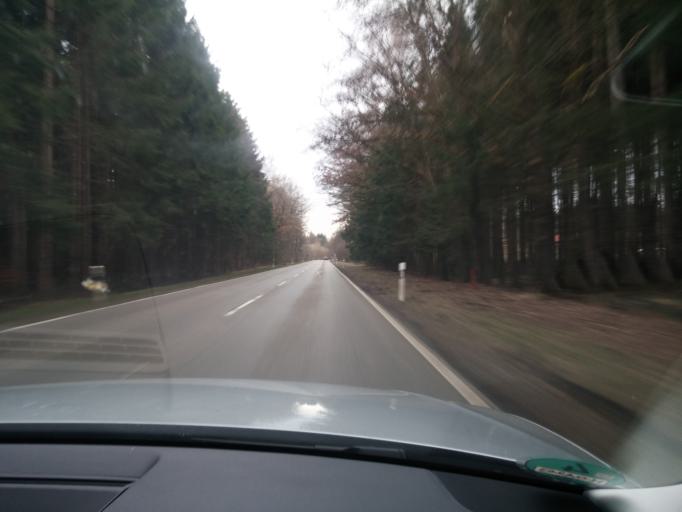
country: DE
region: Bavaria
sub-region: Upper Bavaria
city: Oberpframmern
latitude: 48.0340
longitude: 11.7884
